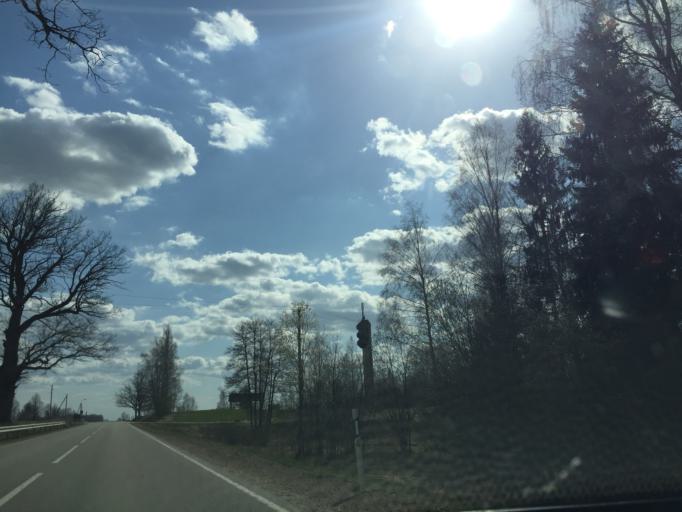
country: LV
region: Skriveri
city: Skriveri
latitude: 56.7419
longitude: 25.1657
